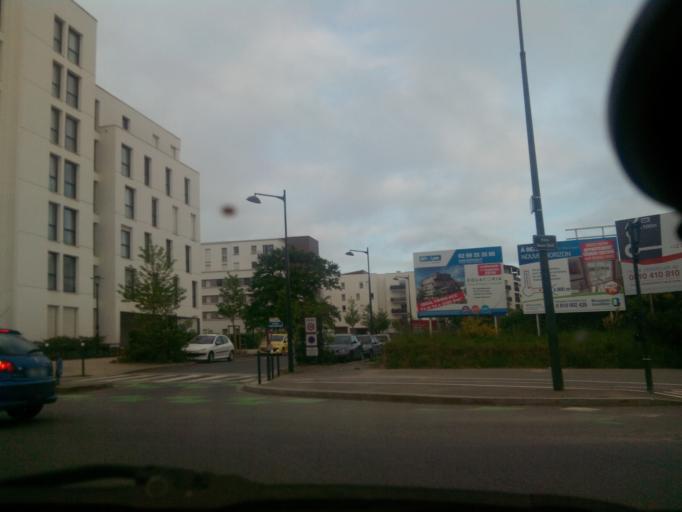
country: FR
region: Brittany
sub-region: Departement d'Ille-et-Vilaine
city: Saint-Gregoire
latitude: 48.1317
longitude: -1.6951
